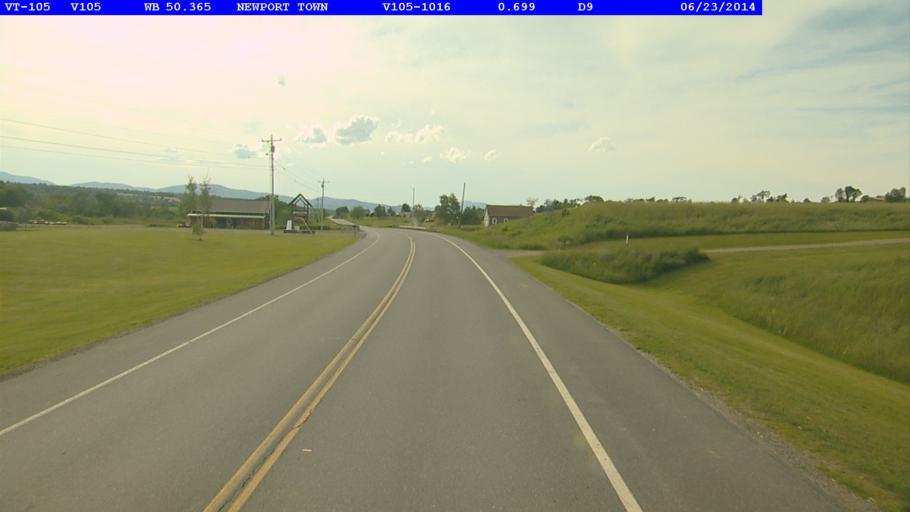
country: US
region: Vermont
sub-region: Orleans County
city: Newport
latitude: 44.9743
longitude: -72.3229
